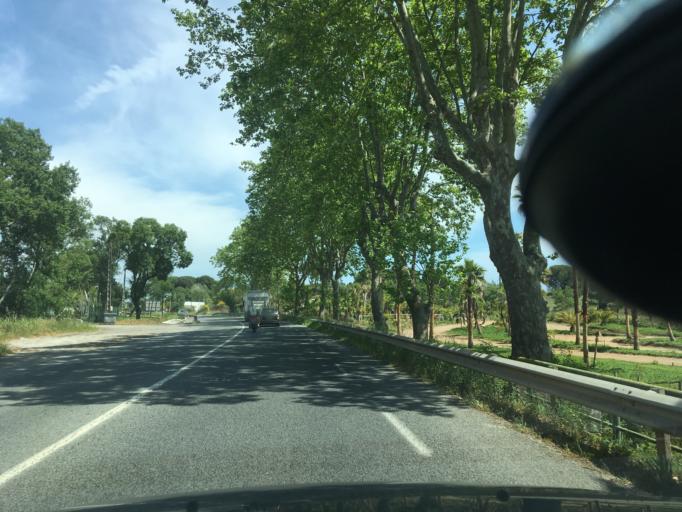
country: FR
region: Provence-Alpes-Cote d'Azur
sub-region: Departement du Var
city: Puget-sur-Argens
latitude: 43.4617
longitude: 6.6525
